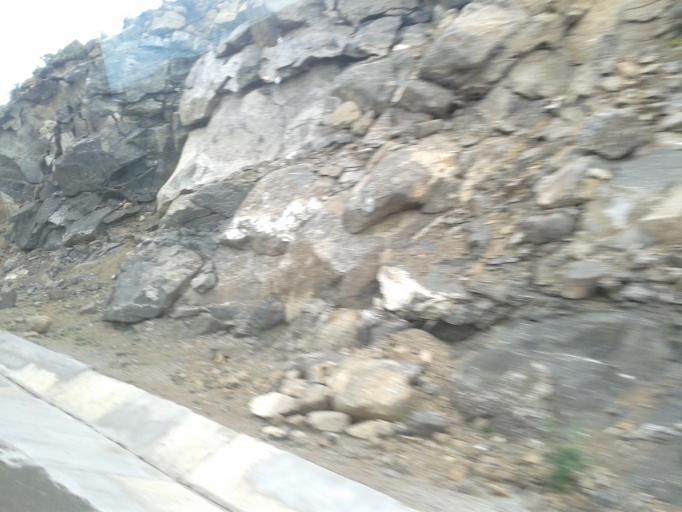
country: LS
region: Maseru
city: Nako
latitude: -29.7635
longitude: 27.9928
